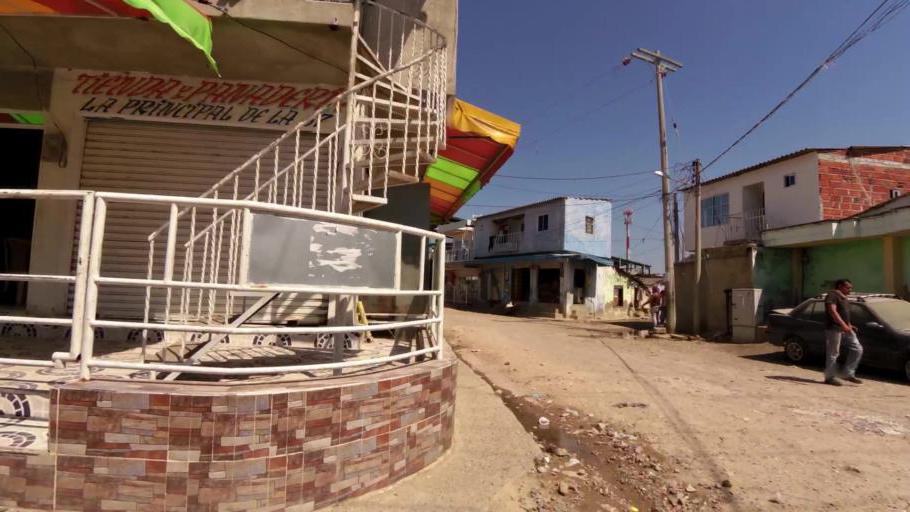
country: CO
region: Bolivar
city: Cartagena
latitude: 10.3843
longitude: -75.5027
